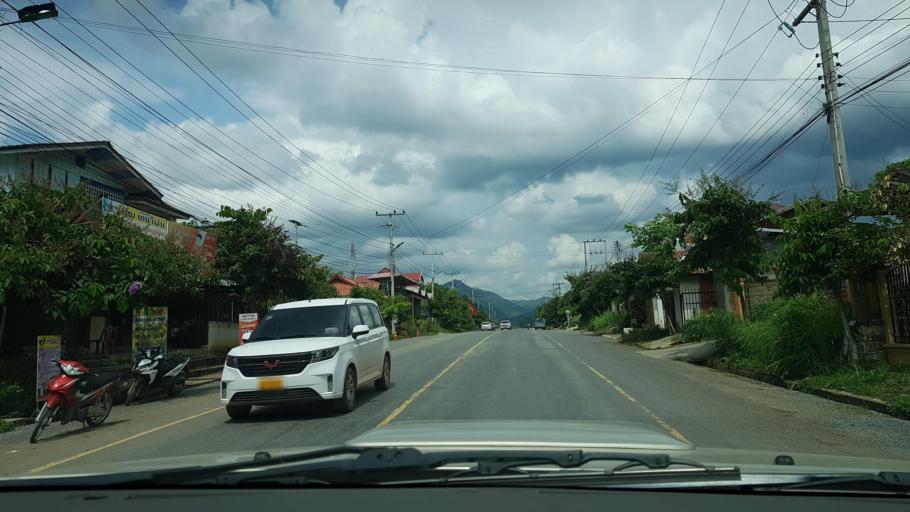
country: LA
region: Loungnamtha
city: Muang Nale
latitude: 20.1474
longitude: 101.4642
